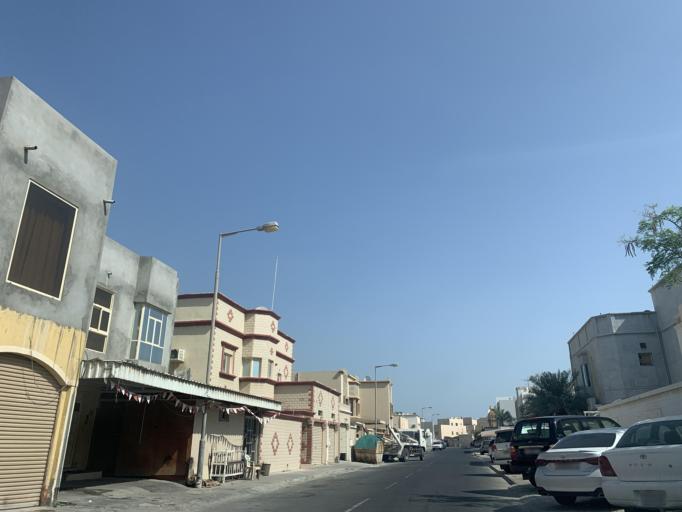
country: BH
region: Central Governorate
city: Madinat Hamad
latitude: 26.1333
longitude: 50.5060
